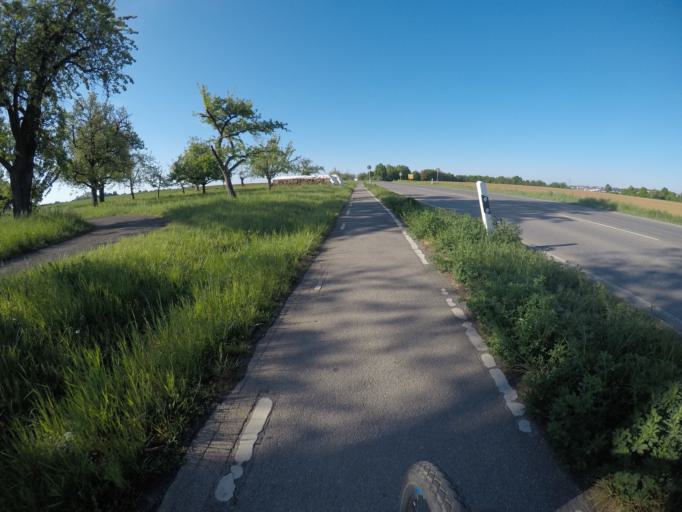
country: DE
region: Baden-Wuerttemberg
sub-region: Regierungsbezirk Stuttgart
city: Filderstadt
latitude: 48.6665
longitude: 9.2295
